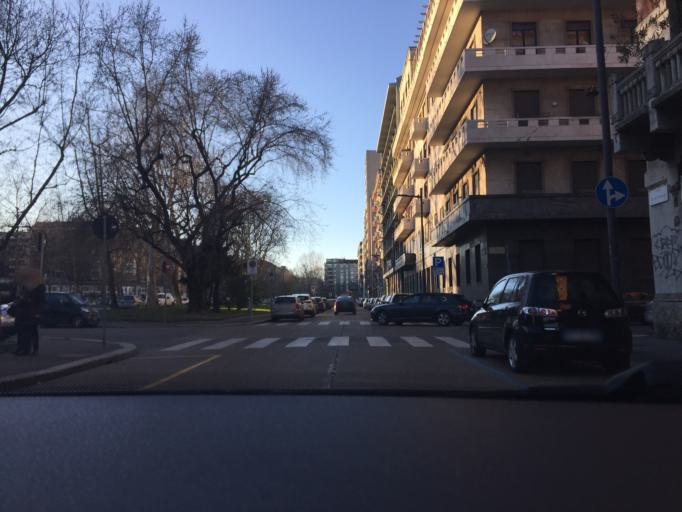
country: IT
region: Lombardy
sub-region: Citta metropolitana di Milano
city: Milano
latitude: 45.4835
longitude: 9.1628
